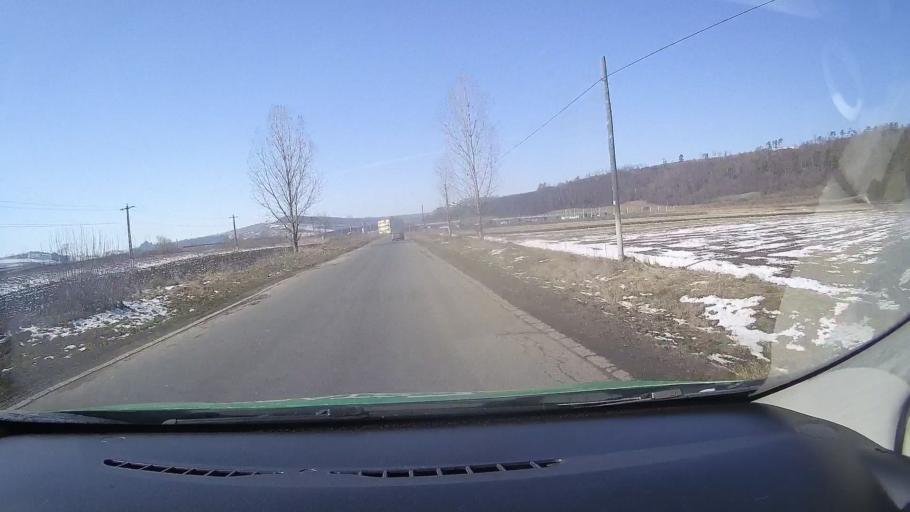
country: RO
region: Brasov
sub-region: Comuna Homorod
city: Homorod
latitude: 46.0386
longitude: 25.2621
